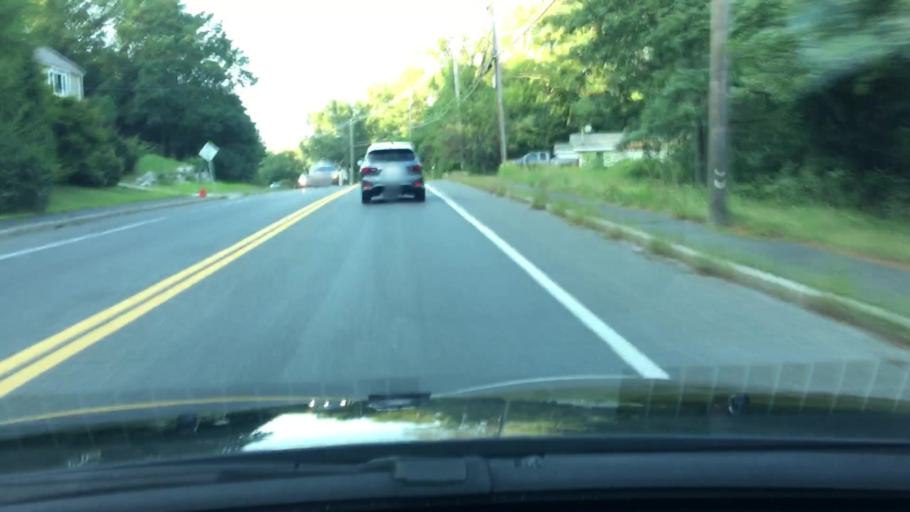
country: US
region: Massachusetts
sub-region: Worcester County
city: Shrewsbury
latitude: 42.3141
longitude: -71.7175
